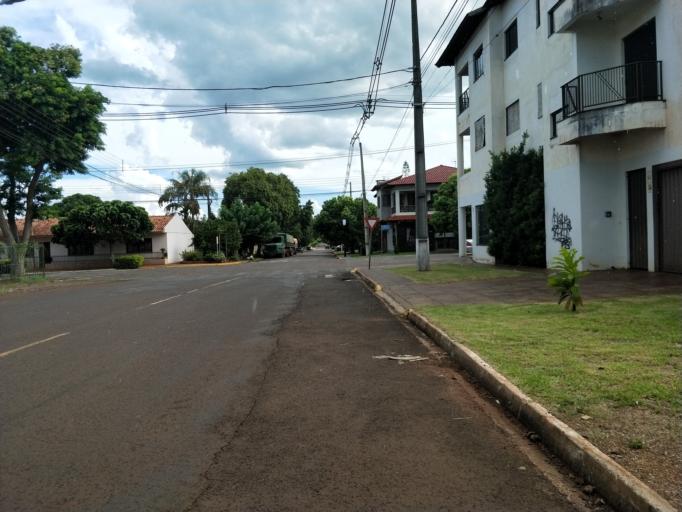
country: BR
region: Parana
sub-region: Marechal Candido Rondon
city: Marechal Candido Rondon
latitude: -24.5534
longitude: -54.0518
